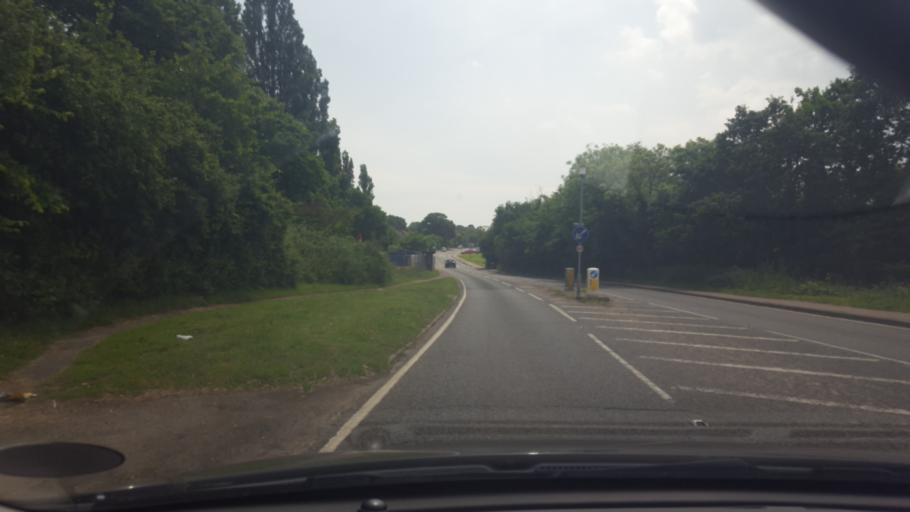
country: GB
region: England
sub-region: Essex
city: Little Clacton
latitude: 51.8515
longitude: 1.1170
